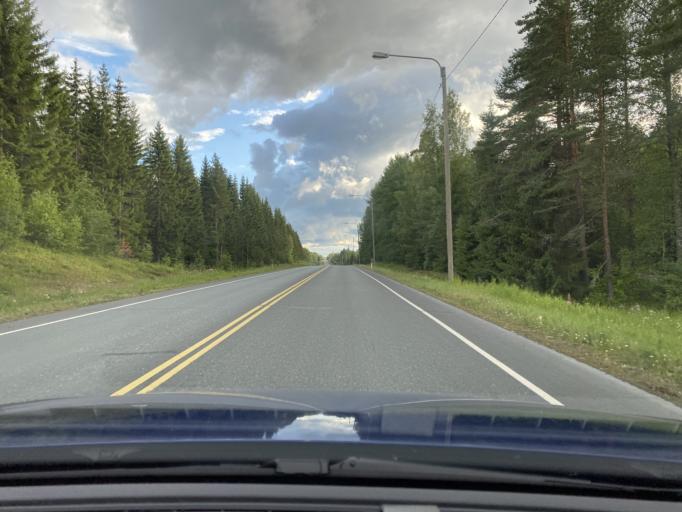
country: FI
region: Haeme
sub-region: Haemeenlinna
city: Renko
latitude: 60.8948
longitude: 24.2714
